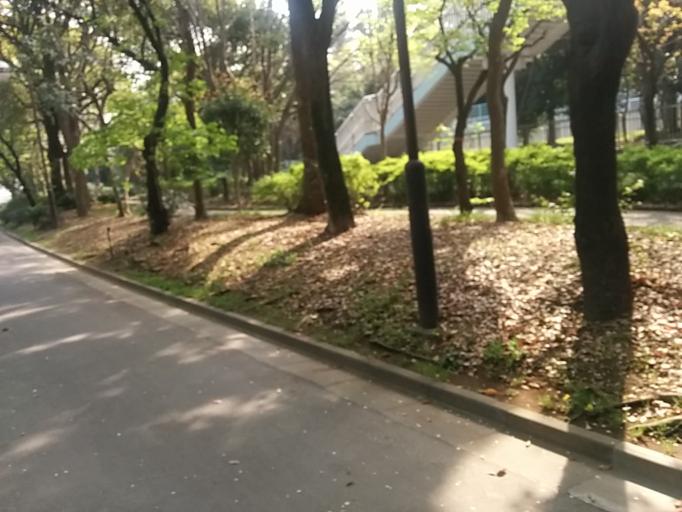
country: JP
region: Tokyo
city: Urayasu
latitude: 35.6490
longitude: 139.8563
